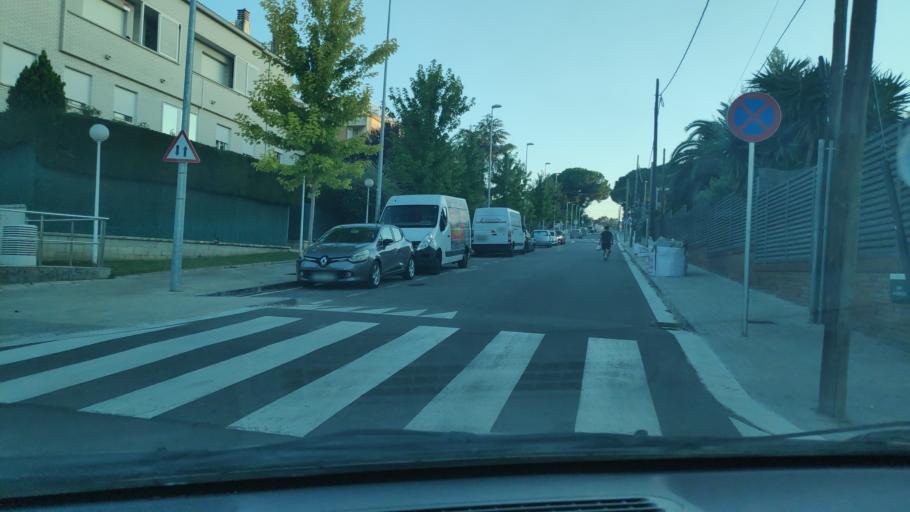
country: ES
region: Catalonia
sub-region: Provincia de Barcelona
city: Cerdanyola del Valles
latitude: 41.4872
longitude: 2.1424
